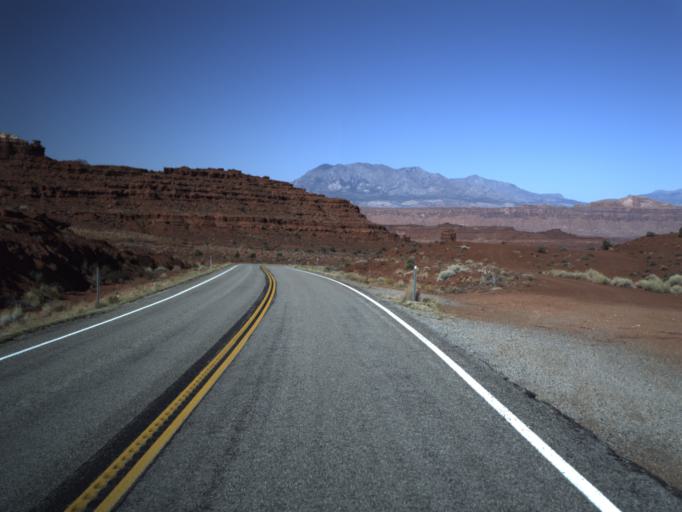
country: US
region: Utah
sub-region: San Juan County
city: Blanding
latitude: 37.8067
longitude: -110.3212
